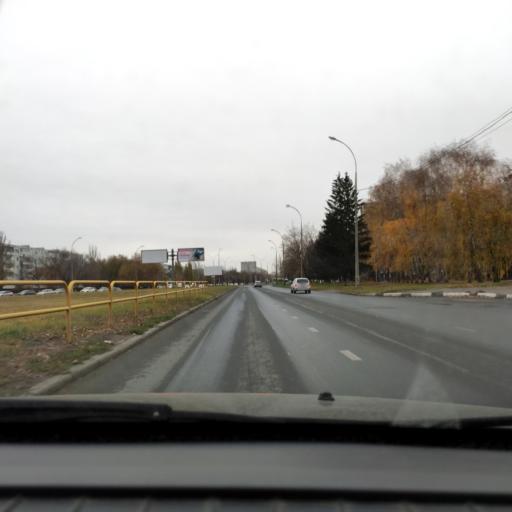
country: RU
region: Samara
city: Tol'yatti
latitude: 53.5283
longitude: 49.2847
